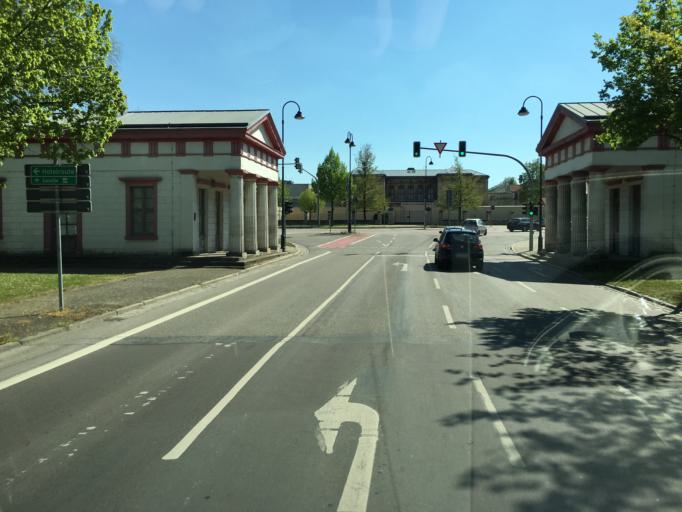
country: DE
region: Saxony-Anhalt
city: Naumburg
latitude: 51.1506
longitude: 11.8051
